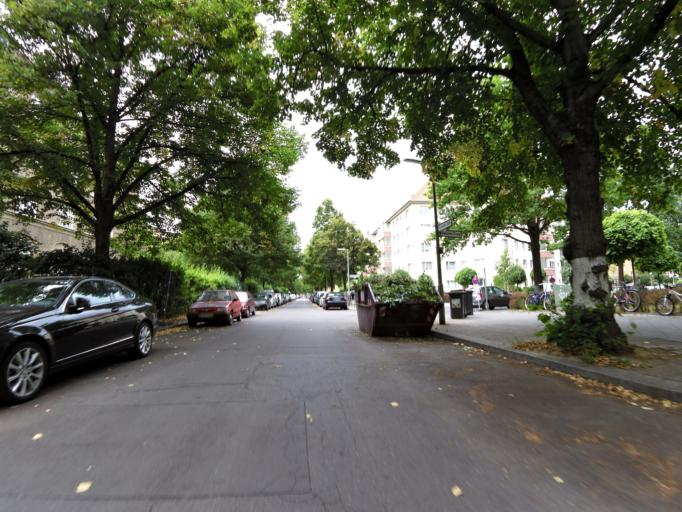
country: DE
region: Berlin
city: Friedenau
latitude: 52.4671
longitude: 13.3180
